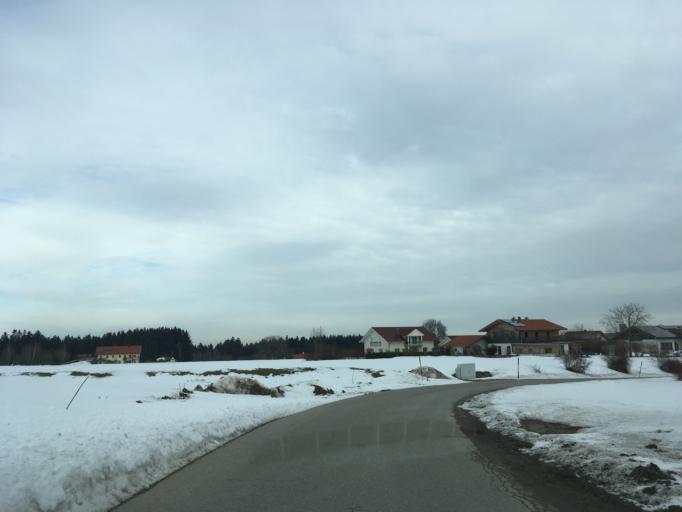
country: DE
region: Bavaria
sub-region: Upper Bavaria
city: Unterreit
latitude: 48.1100
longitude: 12.3721
